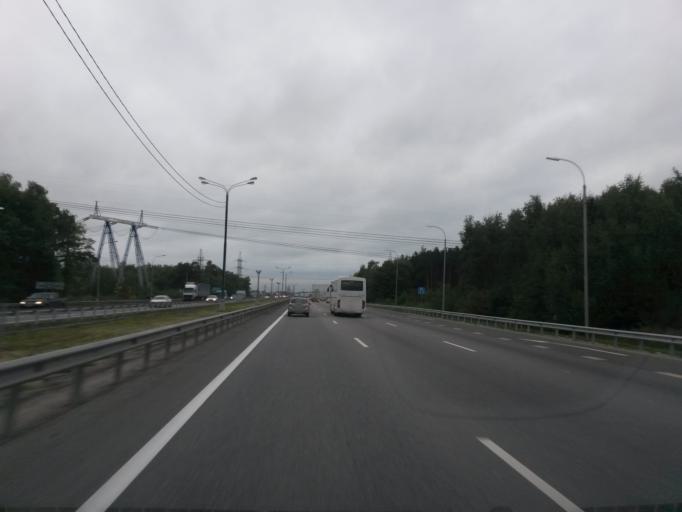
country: RU
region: Moskovskaya
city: Domodedovo
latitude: 55.4549
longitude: 37.7809
